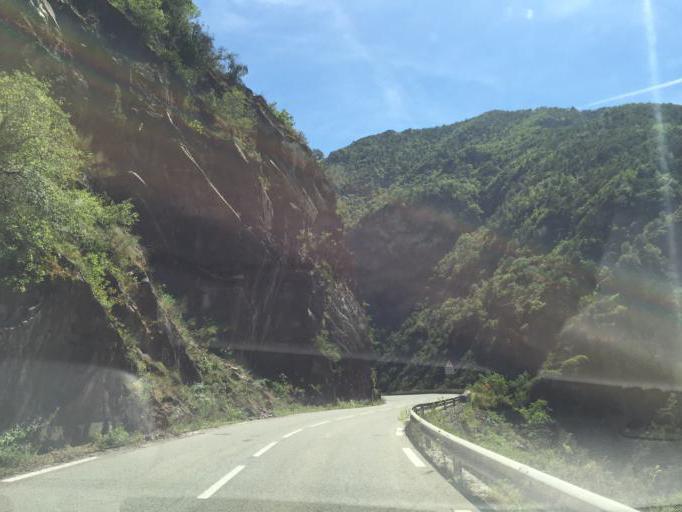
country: FR
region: Provence-Alpes-Cote d'Azur
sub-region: Departement des Alpes-Maritimes
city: Saint-Martin-Vesubie
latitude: 44.0585
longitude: 7.1187
